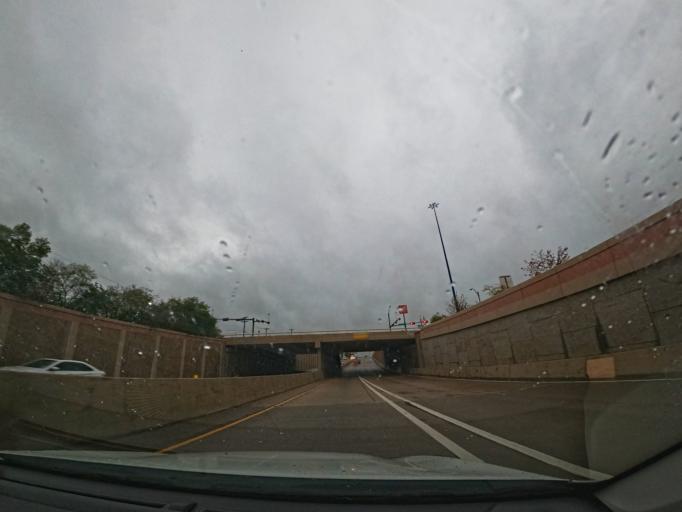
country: US
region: Texas
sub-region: Angelina County
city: Lufkin
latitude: 31.3121
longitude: -94.7221
